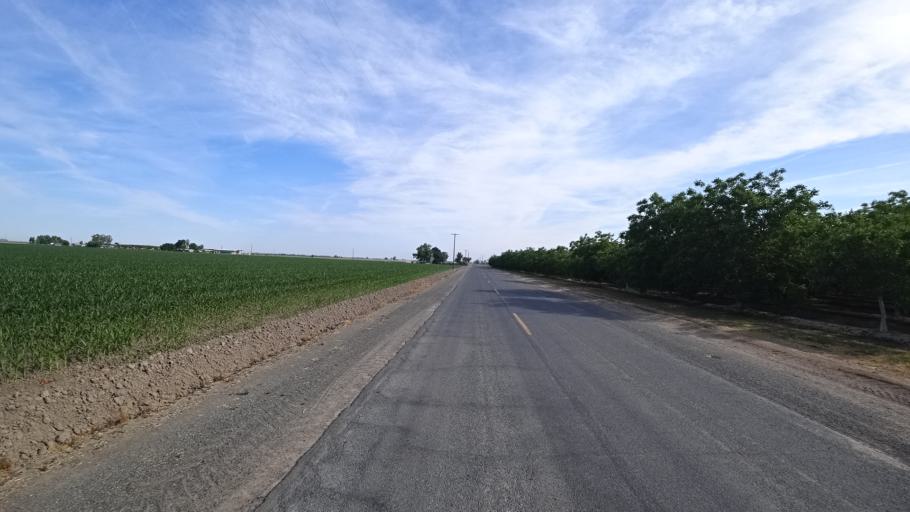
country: US
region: California
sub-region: Kings County
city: Hanford
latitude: 36.3690
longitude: -119.5470
